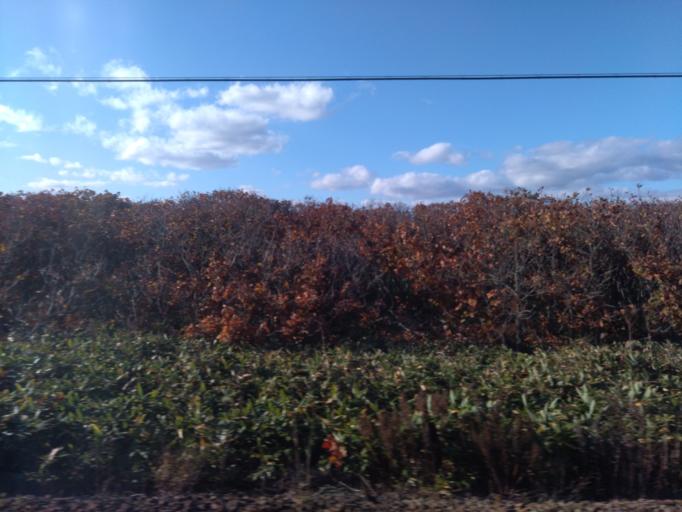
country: JP
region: Hokkaido
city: Niseko Town
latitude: 42.5378
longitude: 140.4032
